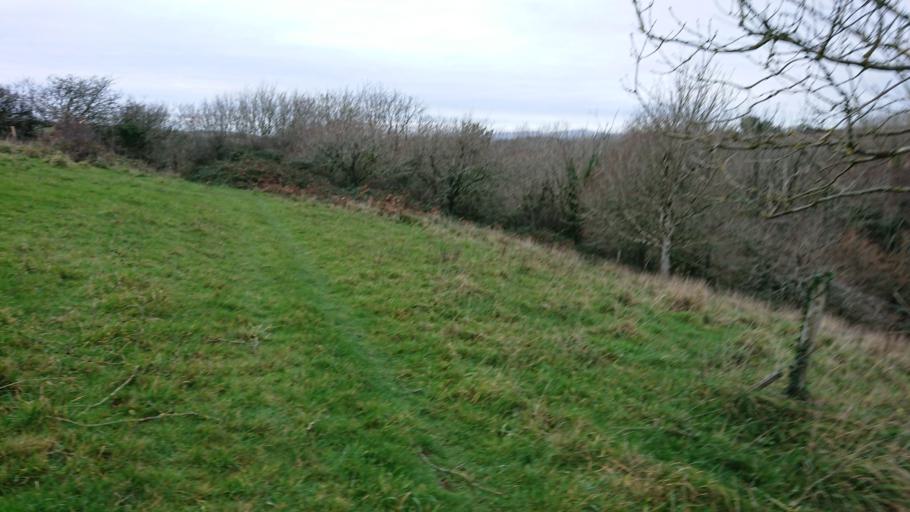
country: GB
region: England
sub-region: Cornwall
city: Fowey
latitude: 50.3385
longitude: -4.5732
